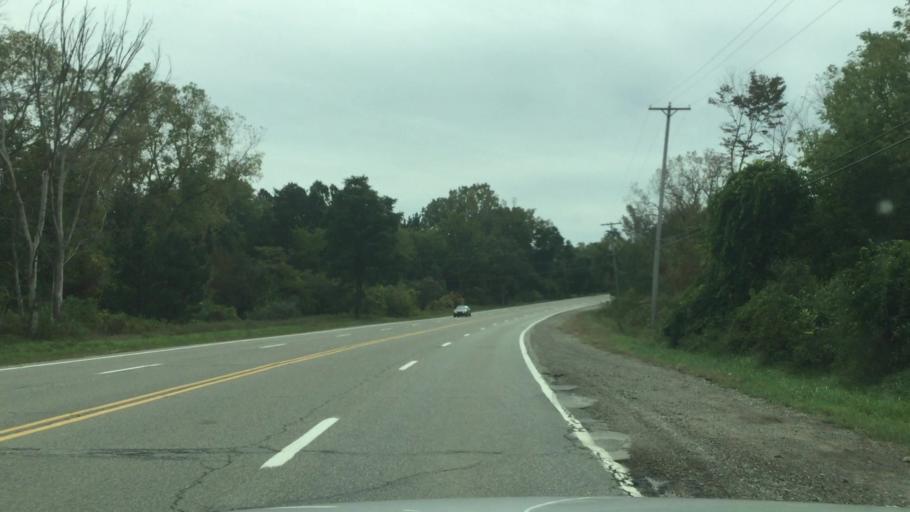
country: US
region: Michigan
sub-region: Oakland County
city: Holly
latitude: 42.8088
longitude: -83.5370
